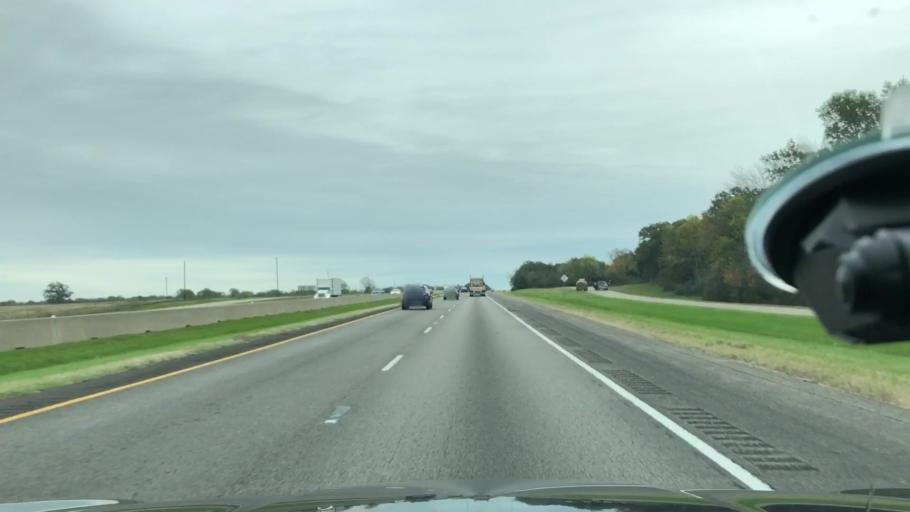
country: US
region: Texas
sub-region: Franklin County
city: Mount Vernon
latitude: 33.1669
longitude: -95.3500
